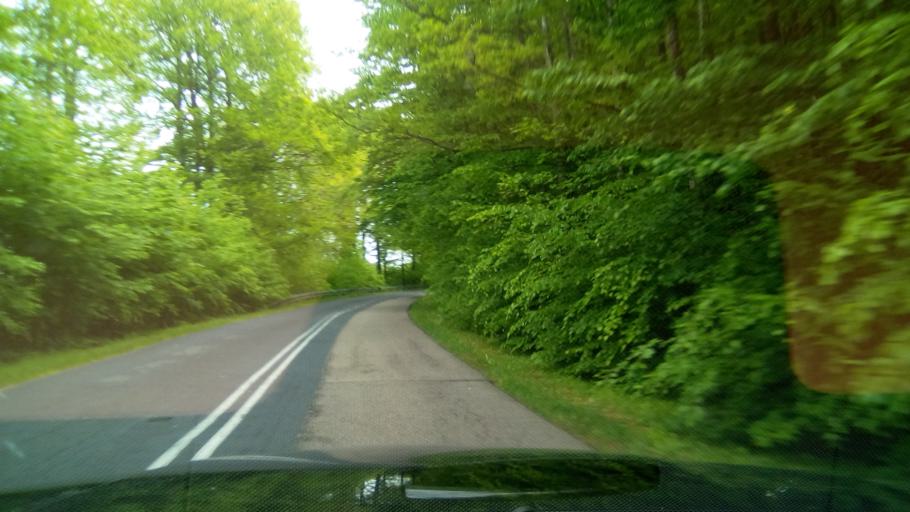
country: PL
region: Pomeranian Voivodeship
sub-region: Powiat bytowski
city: Czarna Dabrowka
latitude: 54.3834
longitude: 17.6555
